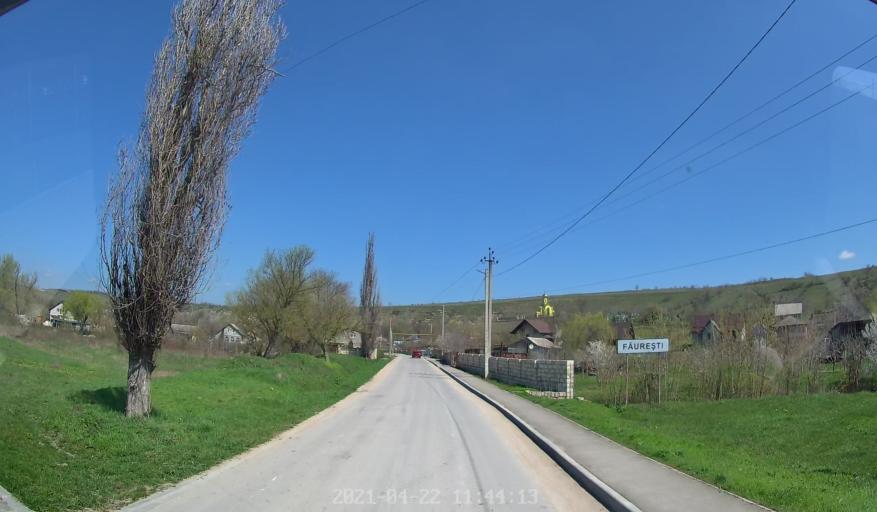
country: MD
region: Chisinau
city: Ciorescu
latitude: 47.1420
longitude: 28.8973
